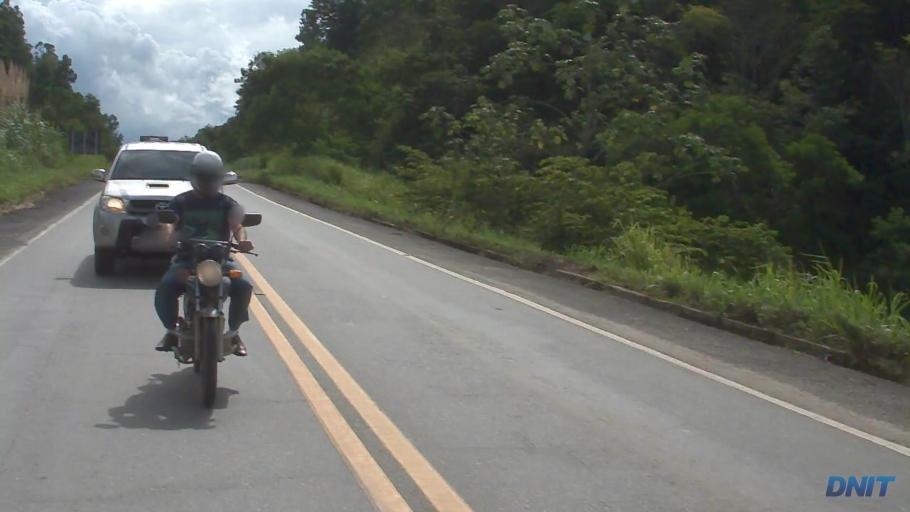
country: BR
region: Minas Gerais
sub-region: Ipaba
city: Ipaba
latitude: -19.3313
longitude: -42.4217
